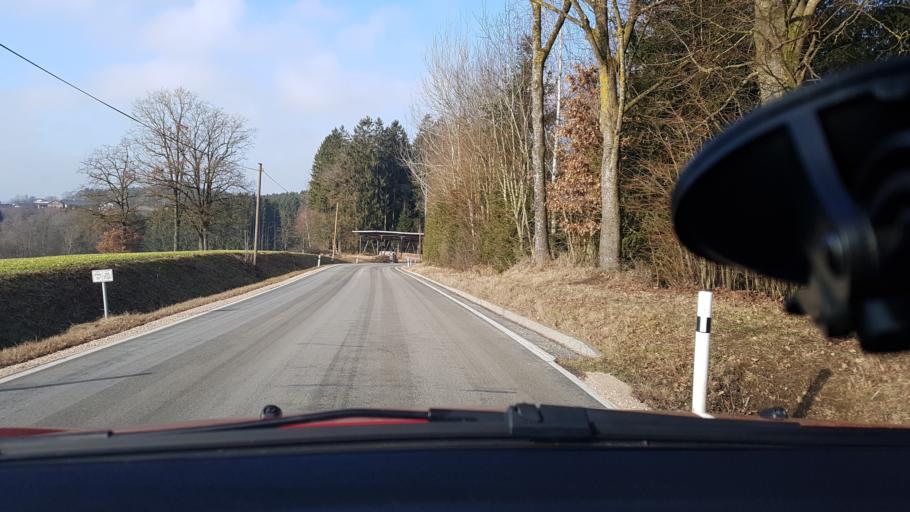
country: DE
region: Bavaria
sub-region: Lower Bavaria
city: Wittibreut
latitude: 48.3307
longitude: 12.9795
